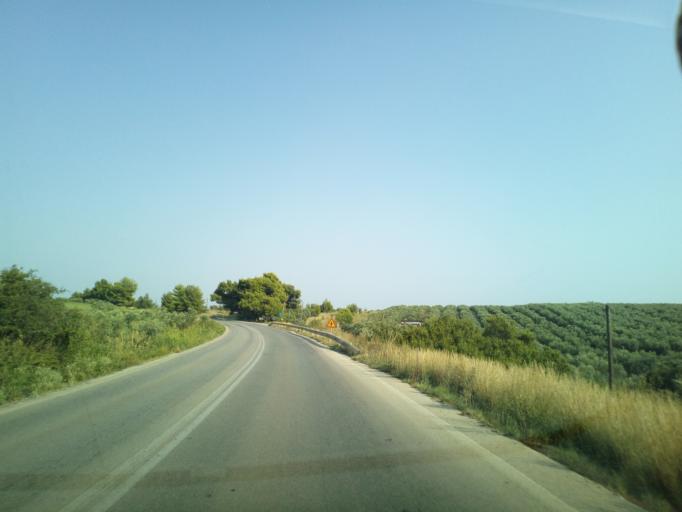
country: GR
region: Central Macedonia
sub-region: Nomos Chalkidikis
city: Ormylia
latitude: 40.2406
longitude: 23.5868
